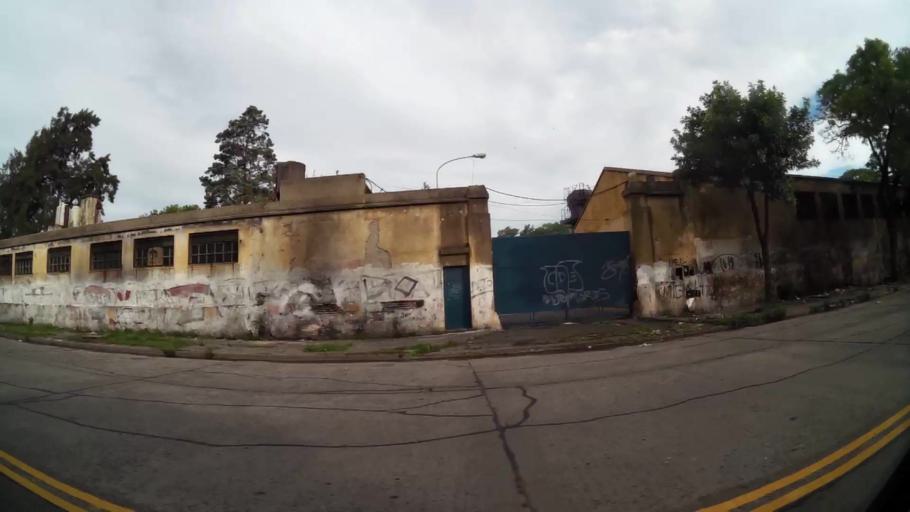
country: AR
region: Buenos Aires F.D.
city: Villa Lugano
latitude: -34.6454
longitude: -58.4473
